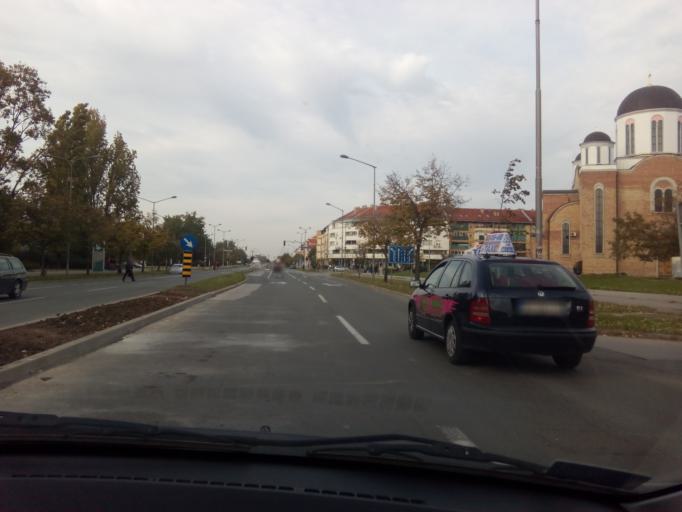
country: RS
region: Autonomna Pokrajina Vojvodina
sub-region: Juznobacki Okrug
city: Novi Sad
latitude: 45.2520
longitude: 19.8050
